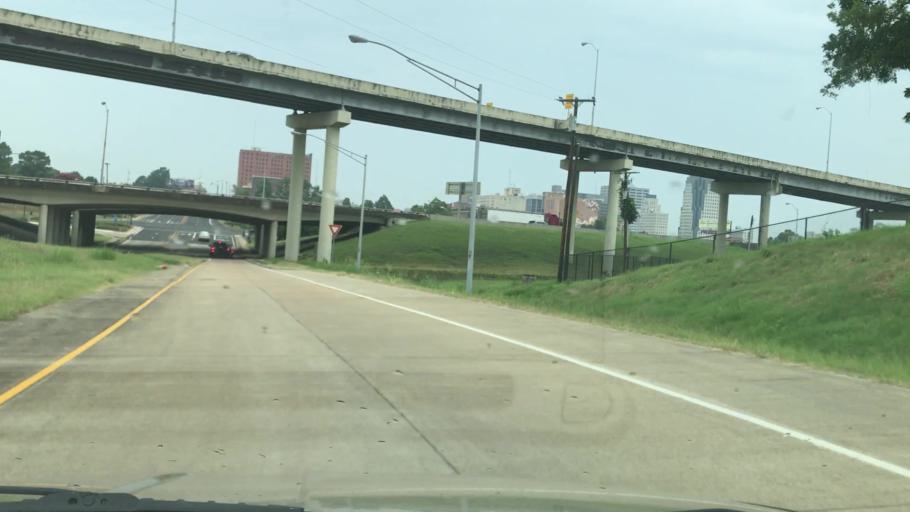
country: US
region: Louisiana
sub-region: Bossier Parish
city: Bossier City
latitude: 32.5040
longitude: -93.7458
